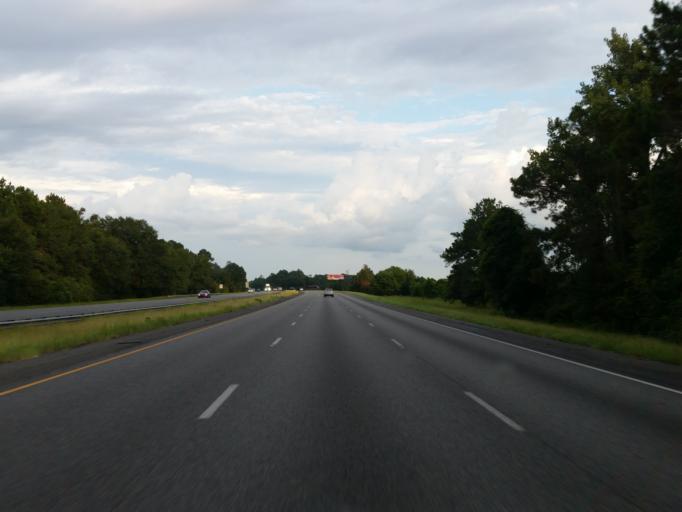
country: US
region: Georgia
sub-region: Echols County
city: Statenville
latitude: 30.6318
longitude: -83.1785
